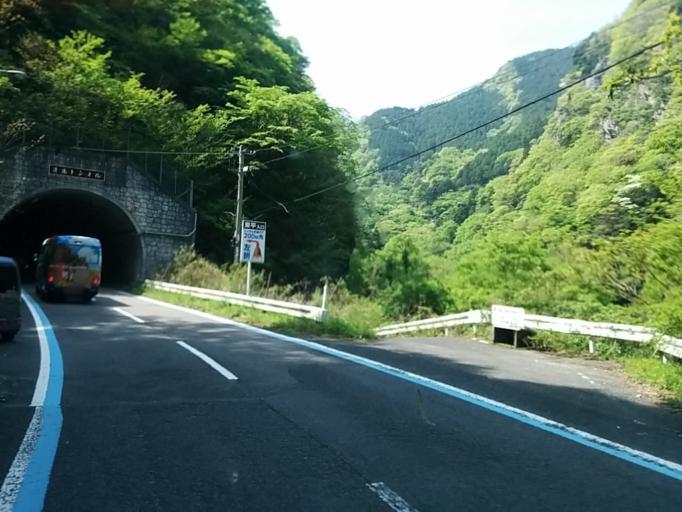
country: JP
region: Ehime
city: Niihama
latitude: 33.8774
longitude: 133.2947
